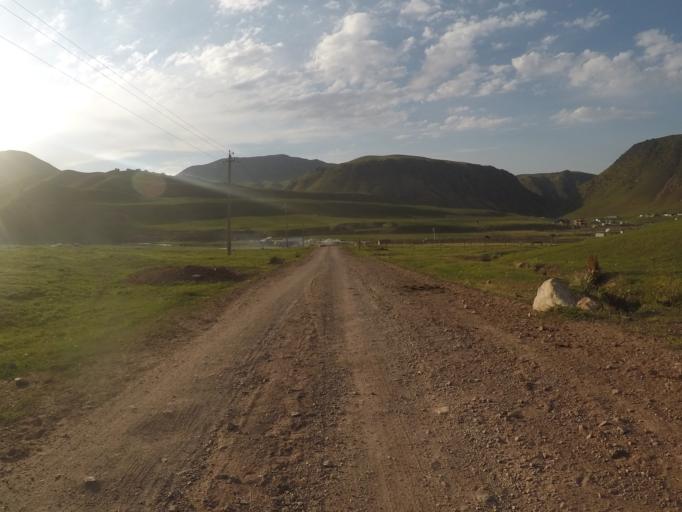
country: KG
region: Chuy
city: Bishkek
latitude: 42.6330
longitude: 74.6170
